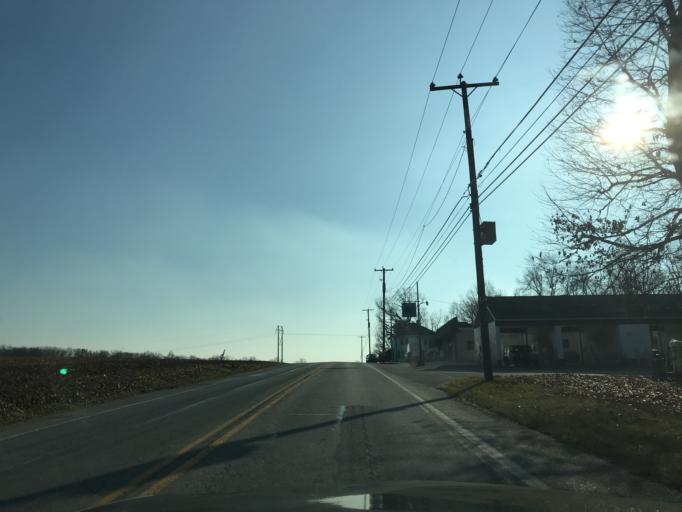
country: US
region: Pennsylvania
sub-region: York County
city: Shrewsbury
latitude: 39.7919
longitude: -76.6786
